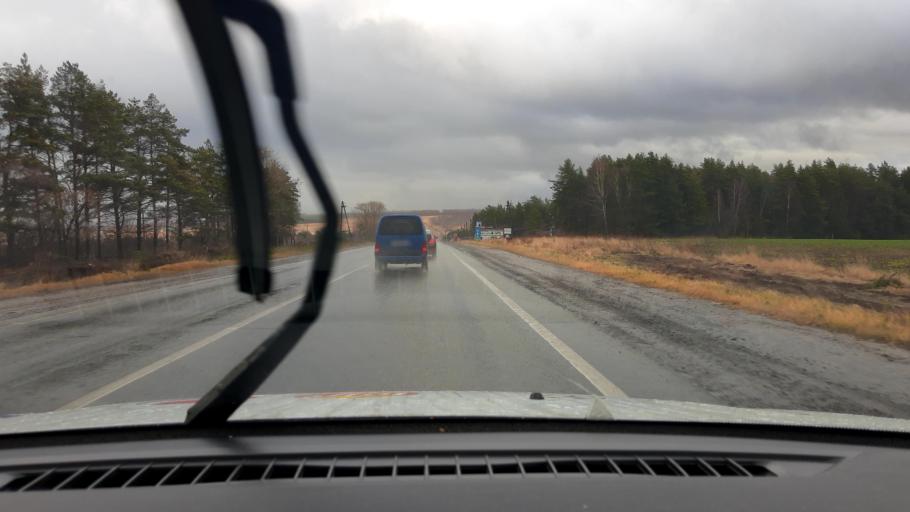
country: RU
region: Nizjnij Novgorod
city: Pamyat' Parizhskoy Kommuny
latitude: 56.0277
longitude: 44.5903
